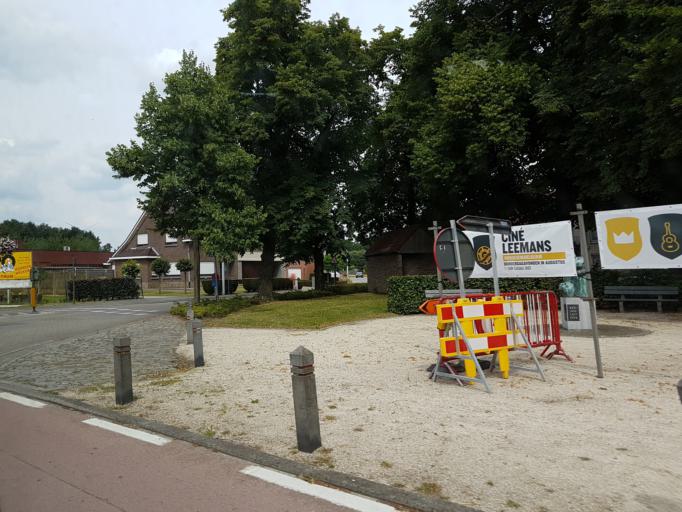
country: BE
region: Flanders
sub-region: Provincie Antwerpen
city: Olen
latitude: 51.1458
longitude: 4.8598
